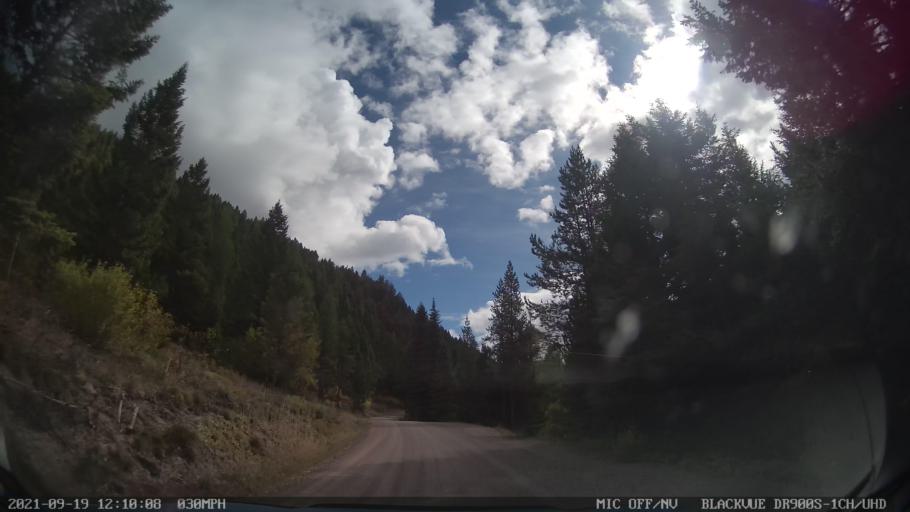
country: US
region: Montana
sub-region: Missoula County
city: Seeley Lake
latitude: 47.1802
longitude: -113.3865
